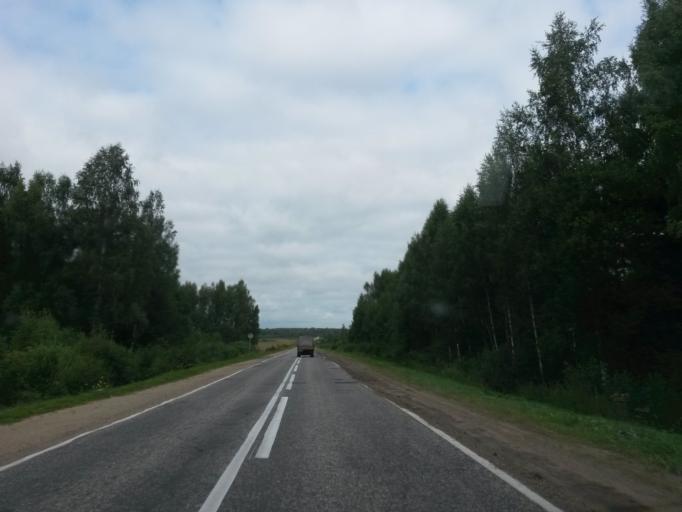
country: RU
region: Jaroslavl
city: Krasnyye Tkachi
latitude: 57.4537
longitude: 39.9121
